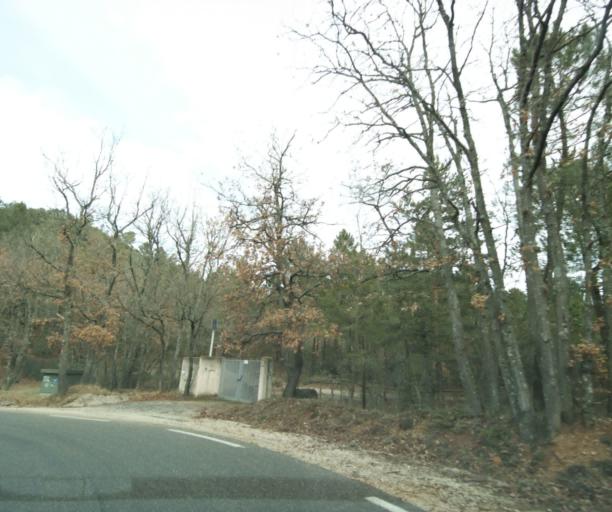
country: FR
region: Provence-Alpes-Cote d'Azur
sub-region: Departement du Var
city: Tourves
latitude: 43.3828
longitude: 5.8991
